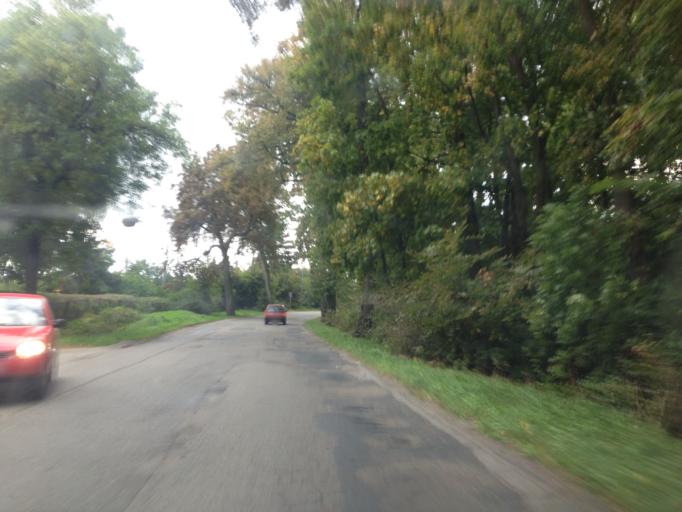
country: PL
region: Pomeranian Voivodeship
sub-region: Powiat kwidzynski
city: Prabuty
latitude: 53.7509
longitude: 19.1819
